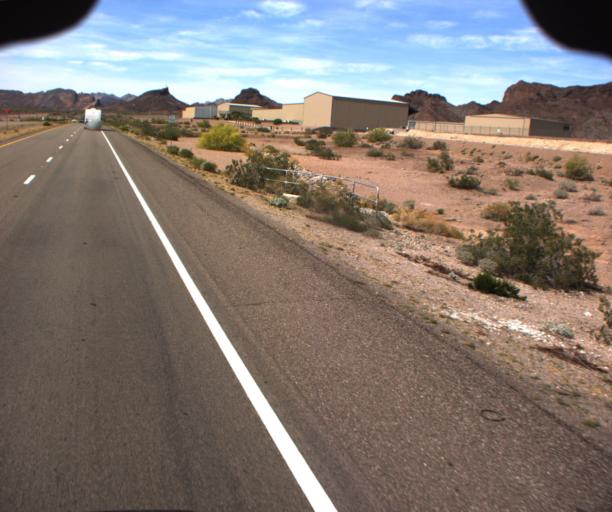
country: US
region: Arizona
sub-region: Mohave County
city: Desert Hills
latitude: 34.5734
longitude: -114.3648
